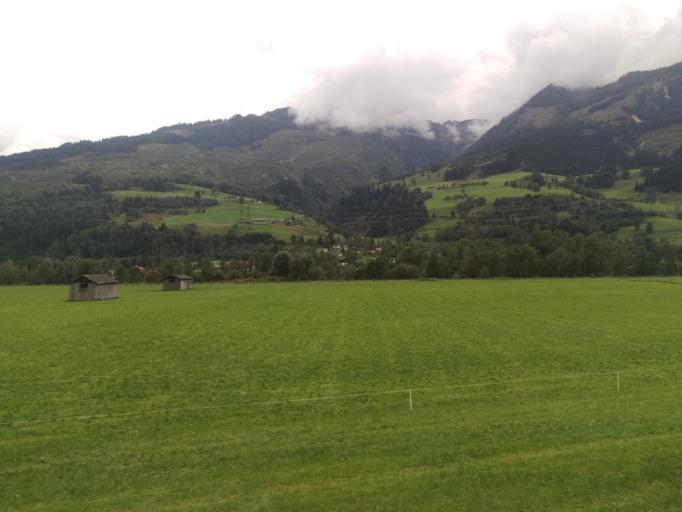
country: AT
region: Salzburg
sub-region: Politischer Bezirk Zell am See
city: Piesendorf
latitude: 47.2843
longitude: 12.6927
